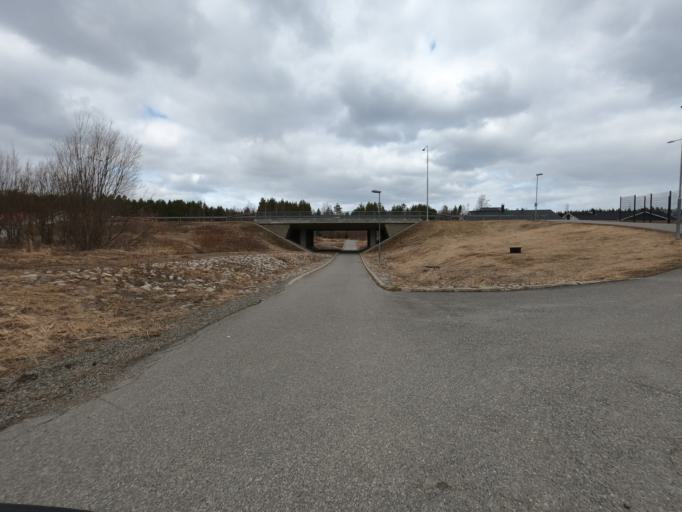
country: FI
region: North Karelia
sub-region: Joensuu
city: Joensuu
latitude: 62.5707
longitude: 29.8130
